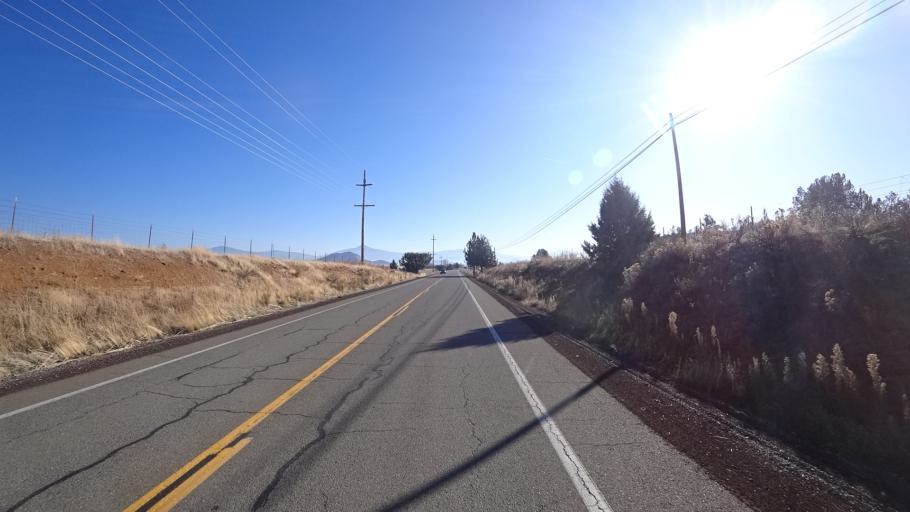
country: US
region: California
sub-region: Siskiyou County
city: Montague
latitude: 41.7106
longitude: -122.5802
